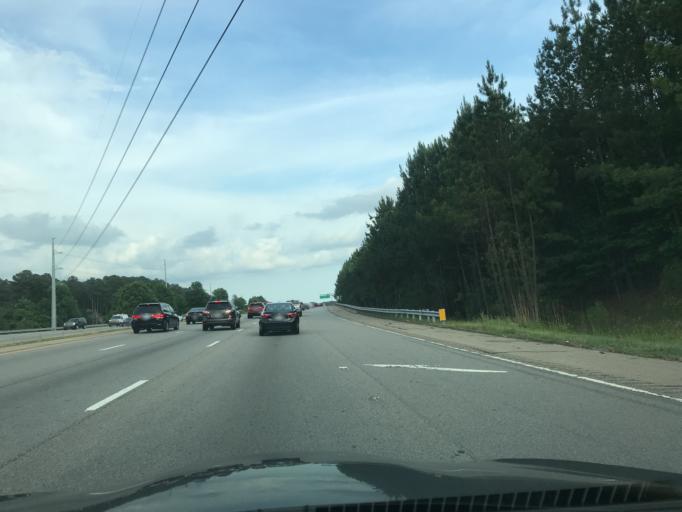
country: US
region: North Carolina
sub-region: Wake County
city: West Raleigh
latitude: 35.9091
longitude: -78.6427
